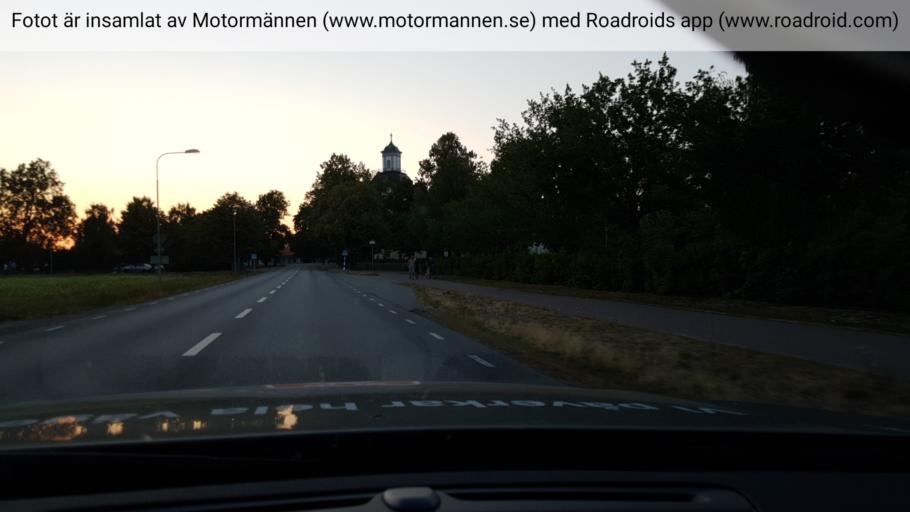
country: SE
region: Uppsala
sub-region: Heby Kommun
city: OEstervala
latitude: 60.1770
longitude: 17.1794
